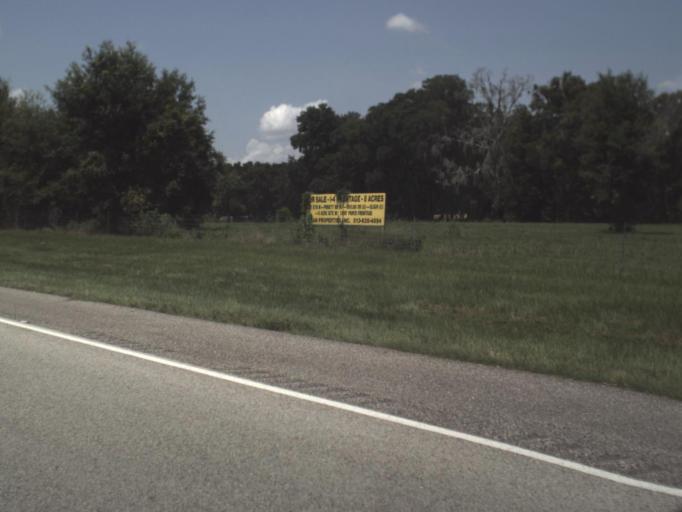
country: US
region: Florida
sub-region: Hillsborough County
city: Seffner
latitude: 28.0113
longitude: -82.2807
